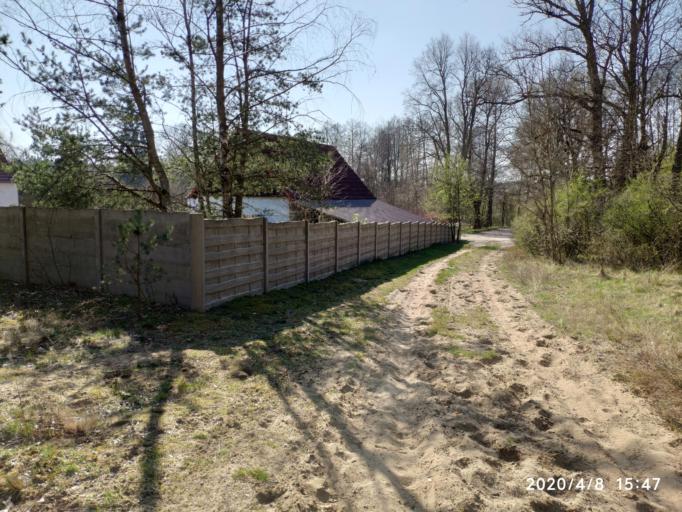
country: PL
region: Lubusz
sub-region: Powiat krosnienski
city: Bobrowice
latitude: 51.9104
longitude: 15.1539
